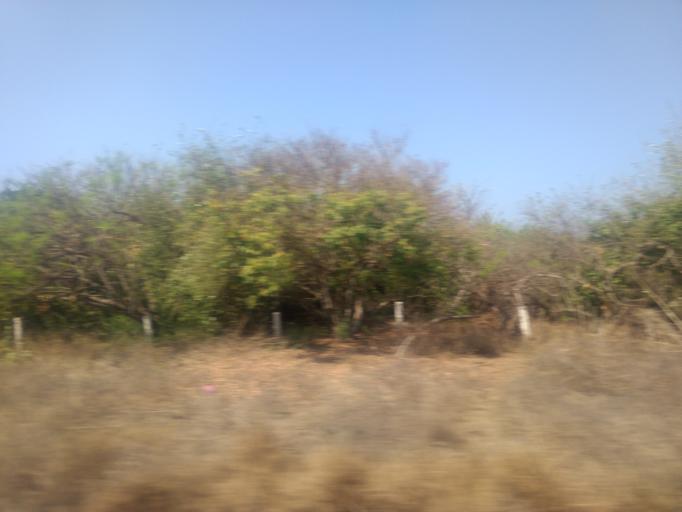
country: MX
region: Colima
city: El Colomo
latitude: 18.9613
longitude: -104.1499
